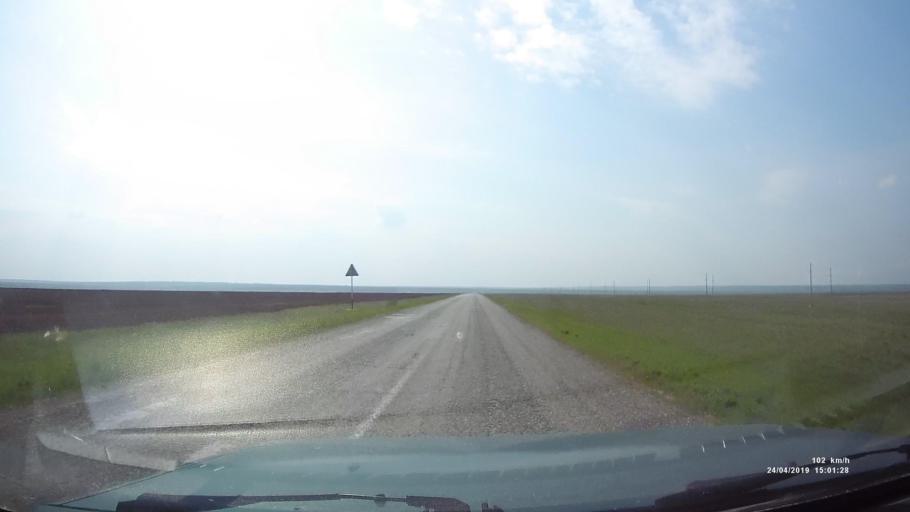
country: RU
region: Rostov
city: Remontnoye
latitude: 46.5659
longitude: 43.5341
